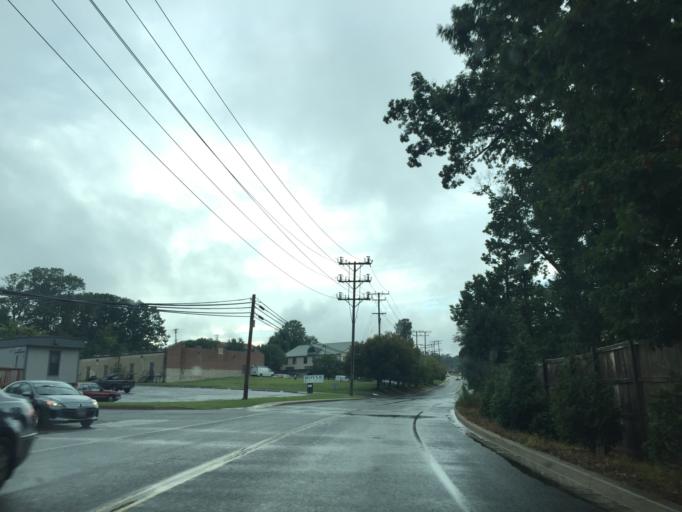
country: US
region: Maryland
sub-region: Harford County
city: Bel Air South
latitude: 39.4754
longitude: -76.3066
